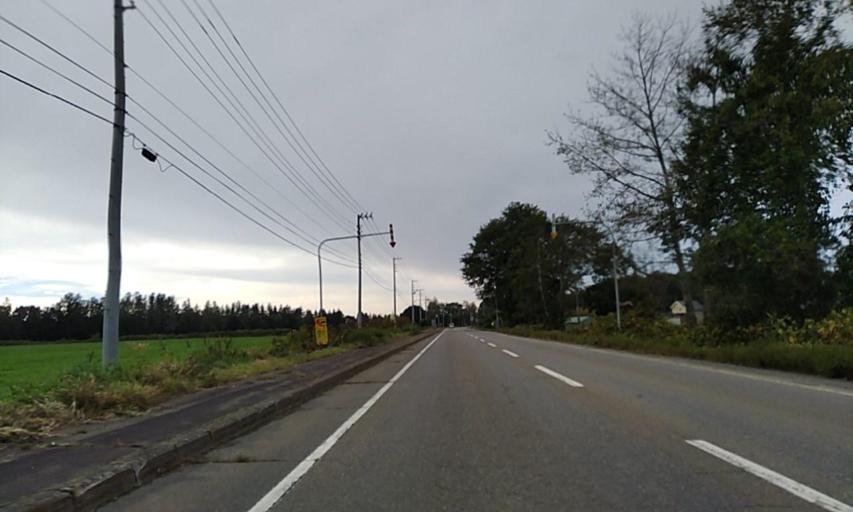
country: JP
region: Hokkaido
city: Obihiro
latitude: 42.7350
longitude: 143.1562
